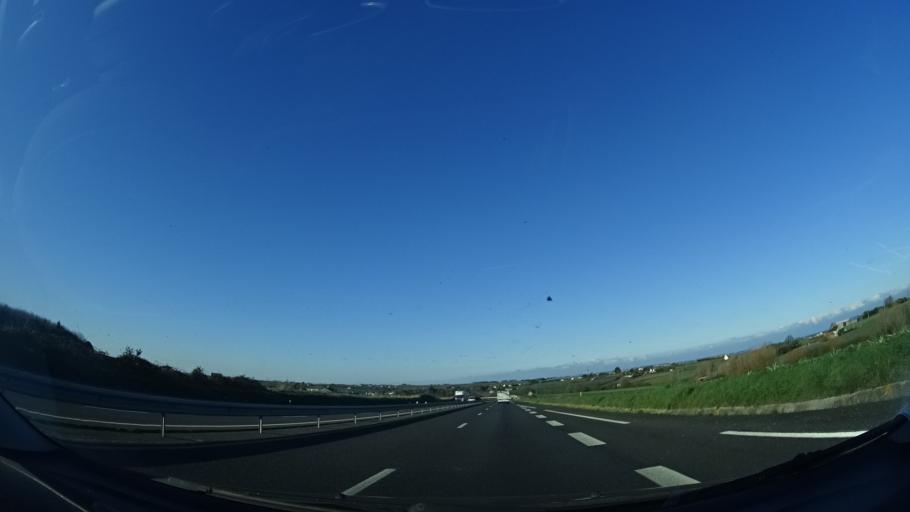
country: FR
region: Brittany
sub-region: Departement du Finistere
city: Henvic
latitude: 48.6393
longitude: -3.9290
